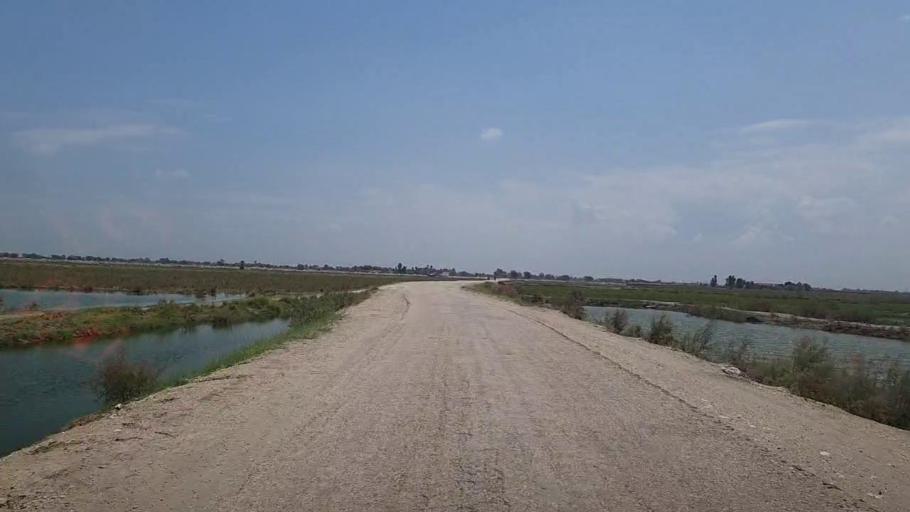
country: PK
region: Sindh
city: Kandhkot
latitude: 28.2797
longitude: 69.1730
